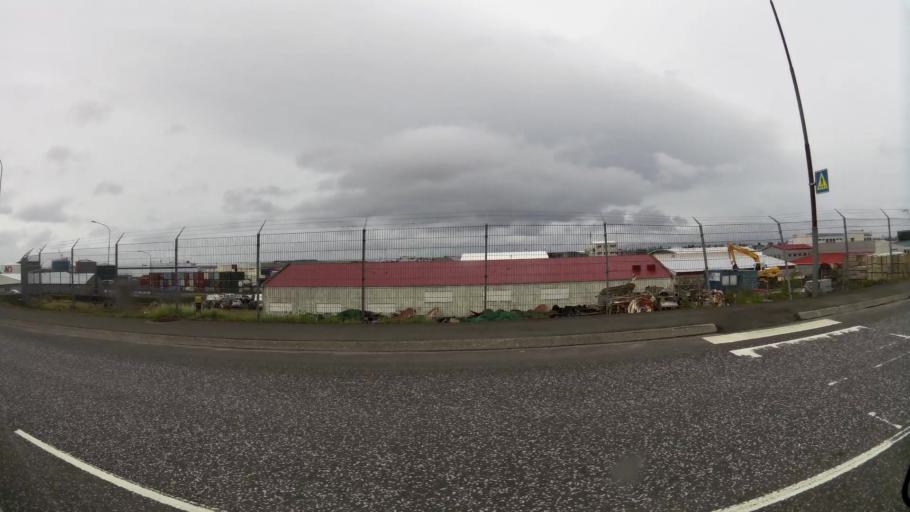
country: IS
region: Capital Region
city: Hafnarfjoerdur
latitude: 64.0625
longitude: -21.9694
